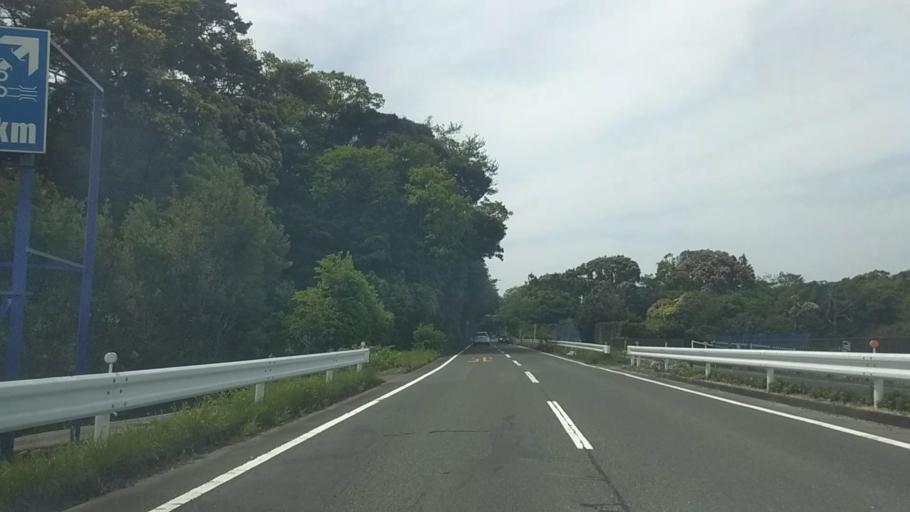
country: JP
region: Shizuoka
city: Kosai-shi
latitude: 34.7712
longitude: 137.5565
